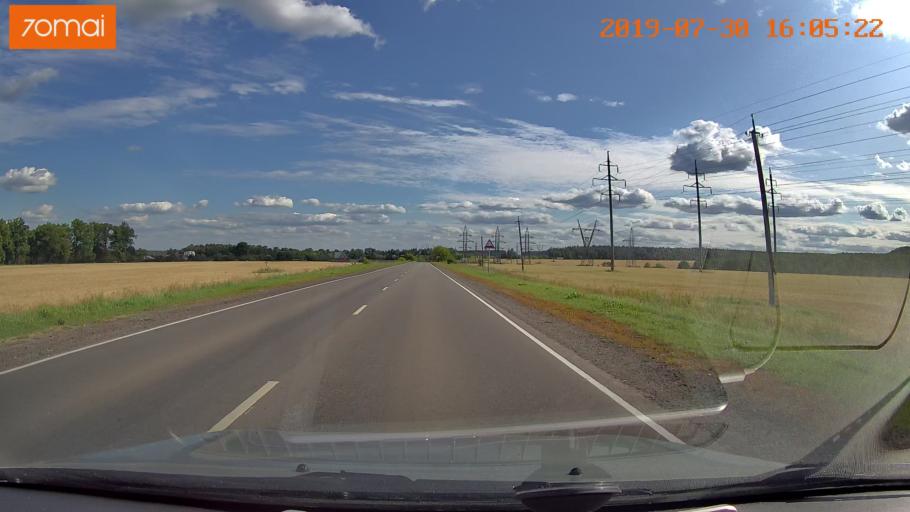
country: RU
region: Moskovskaya
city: Peski
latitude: 55.2665
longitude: 38.7148
